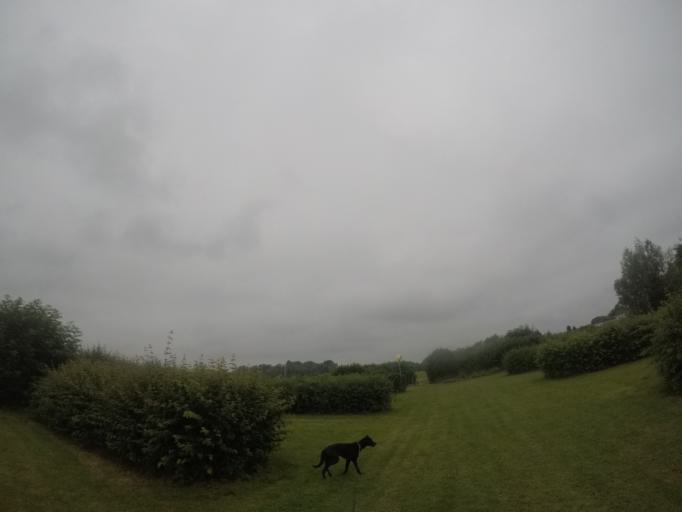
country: NL
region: Gelderland
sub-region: Gemeente Rheden
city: Rheden
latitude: 51.9930
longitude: 6.0259
